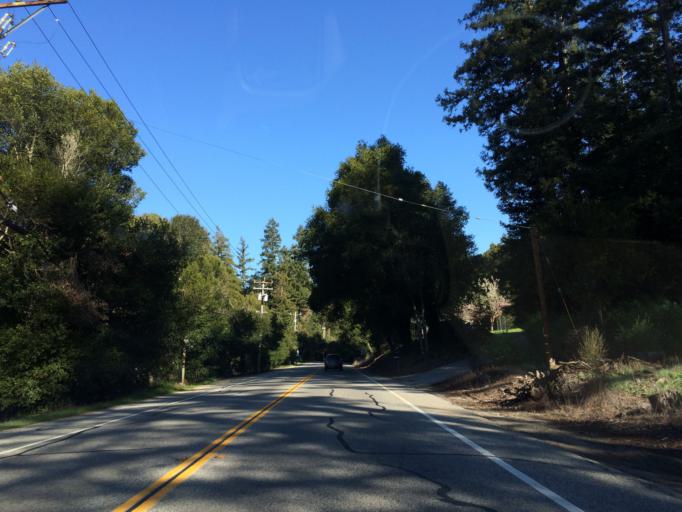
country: US
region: California
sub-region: Santa Cruz County
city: Boulder Creek
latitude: 37.1754
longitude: -122.1386
